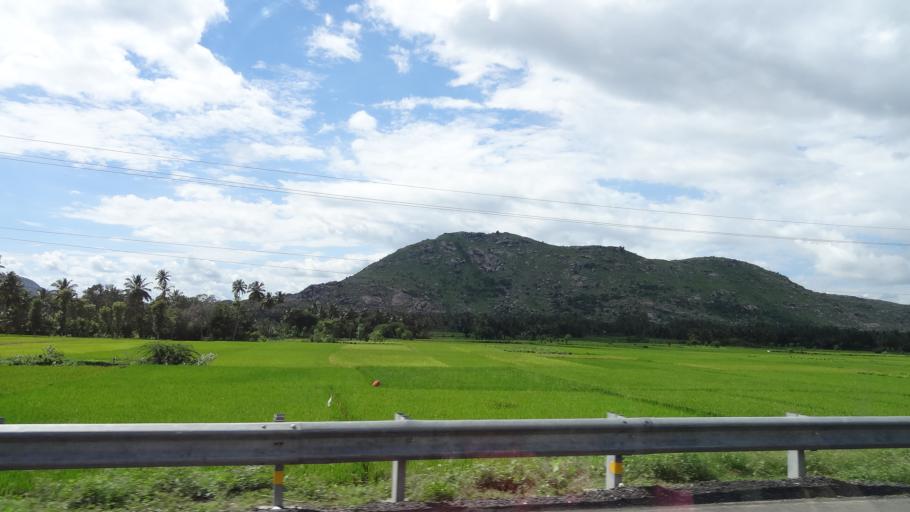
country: IN
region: Tamil Nadu
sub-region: Krishnagiri
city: Krishnagiri
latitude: 12.4716
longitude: 78.2143
